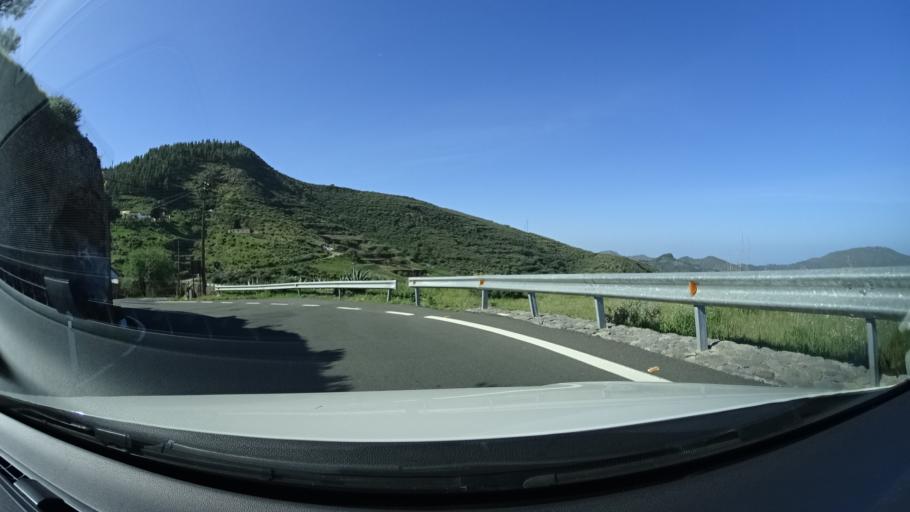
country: ES
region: Canary Islands
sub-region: Provincia de Las Palmas
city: Artenara
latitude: 28.0258
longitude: -15.6342
